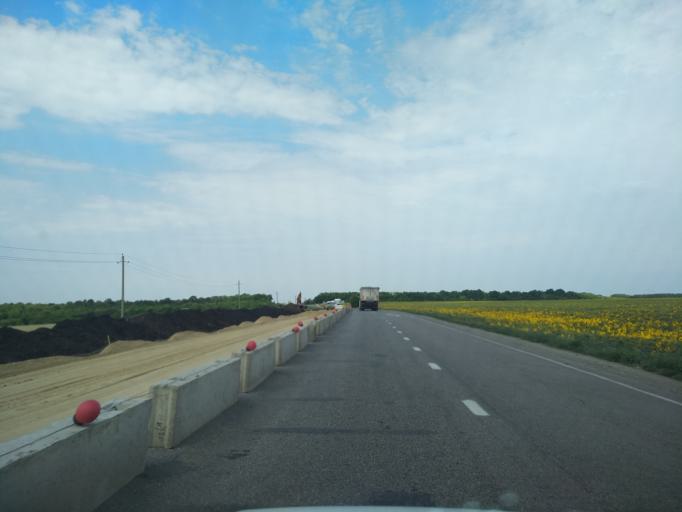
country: RU
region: Voronezj
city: Verkhnyaya Khava
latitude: 51.6777
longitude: 39.8012
